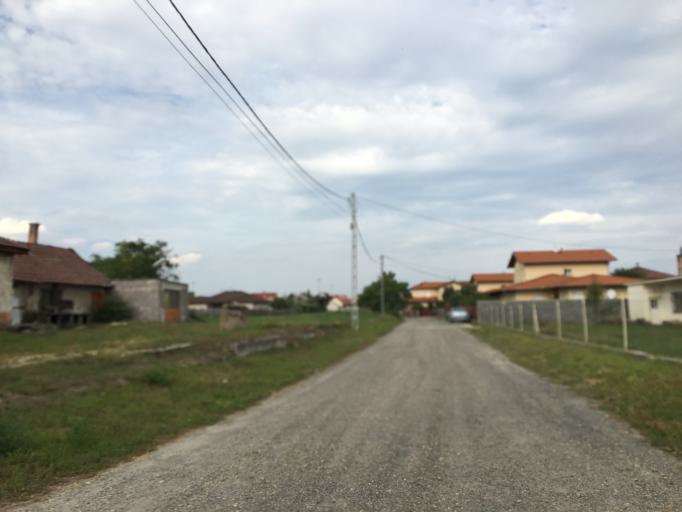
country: HU
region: Pest
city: Szigetszentmiklos
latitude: 47.3497
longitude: 19.0514
